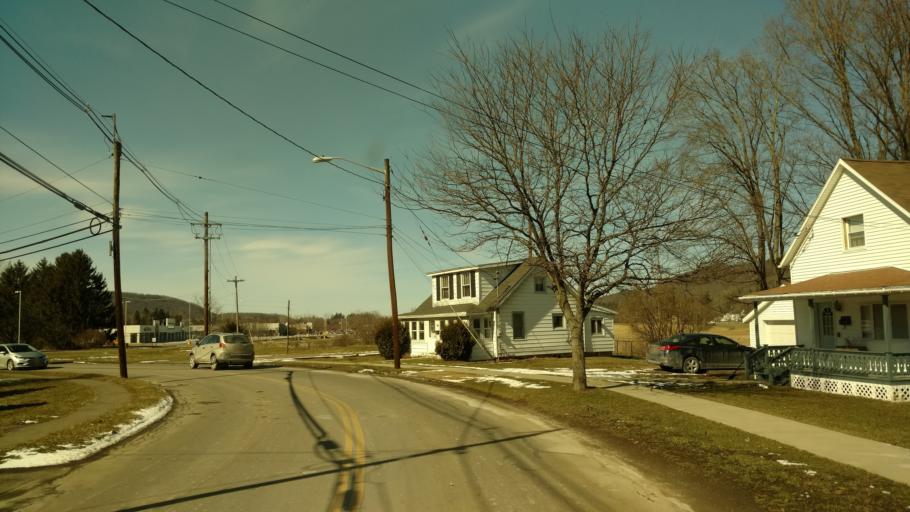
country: US
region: New York
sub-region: Allegany County
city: Wellsville
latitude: 42.1227
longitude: -77.9593
